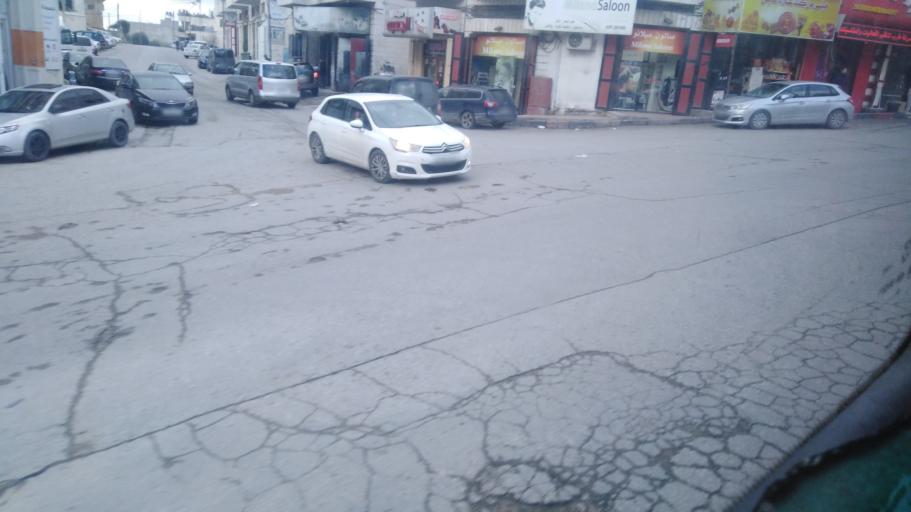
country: PS
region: West Bank
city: Hebron
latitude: 31.5291
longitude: 35.0819
